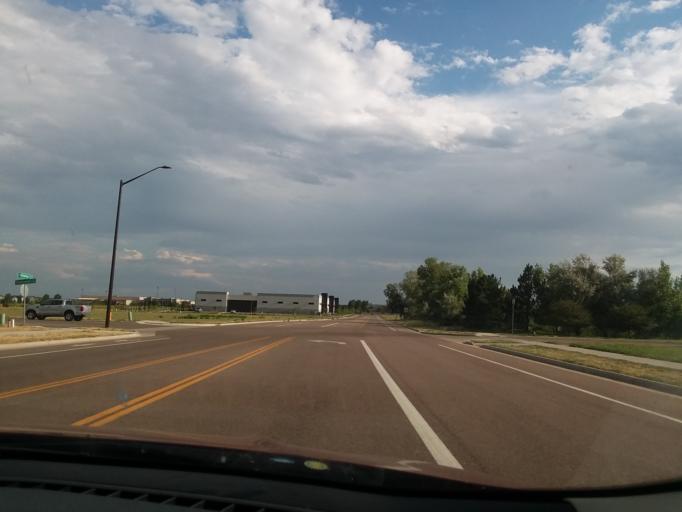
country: US
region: Colorado
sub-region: Larimer County
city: Fort Collins
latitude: 40.5219
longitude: -105.0156
